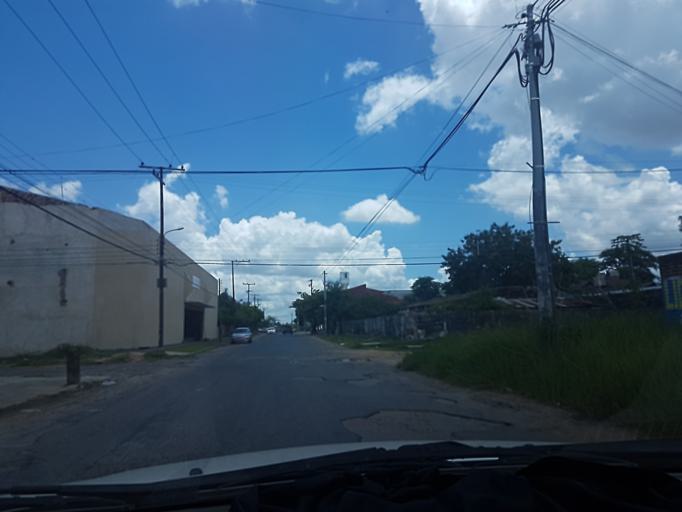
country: PY
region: Central
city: Fernando de la Mora
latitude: -25.2825
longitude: -57.5376
